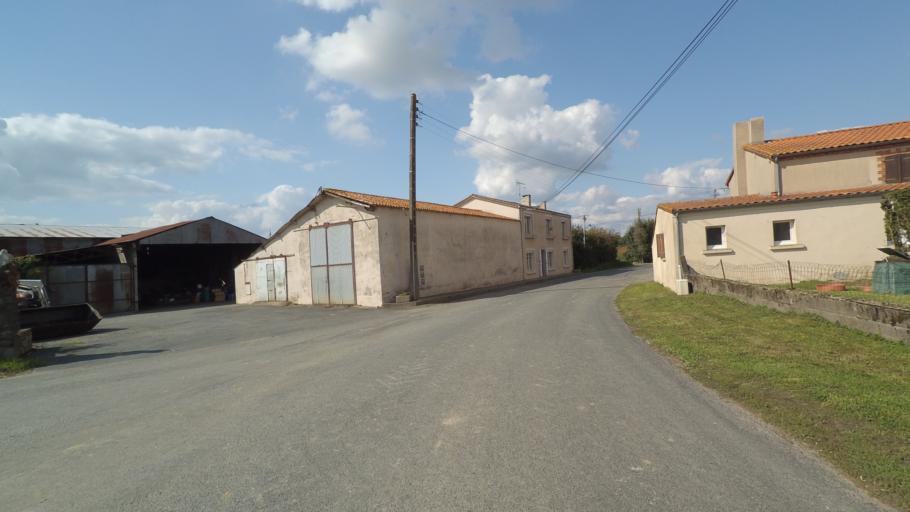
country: FR
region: Pays de la Loire
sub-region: Departement de la Vendee
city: Bouffere
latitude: 46.9584
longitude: -1.3801
